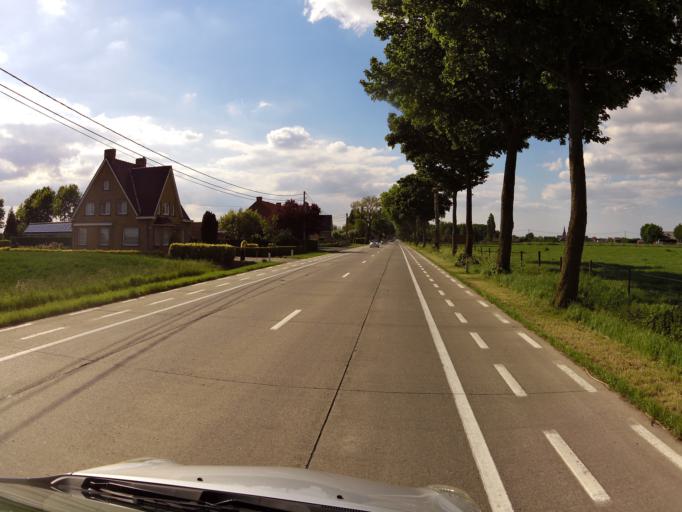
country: BE
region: Flanders
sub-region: Provincie West-Vlaanderen
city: Poperinge
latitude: 50.9242
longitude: 2.7496
